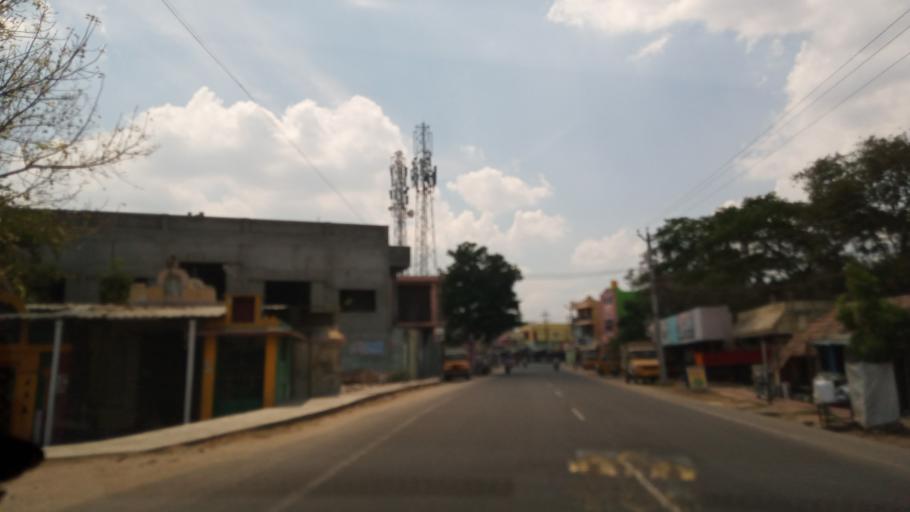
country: IN
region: Tamil Nadu
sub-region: Vellore
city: Walajapet
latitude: 12.9242
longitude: 79.3713
